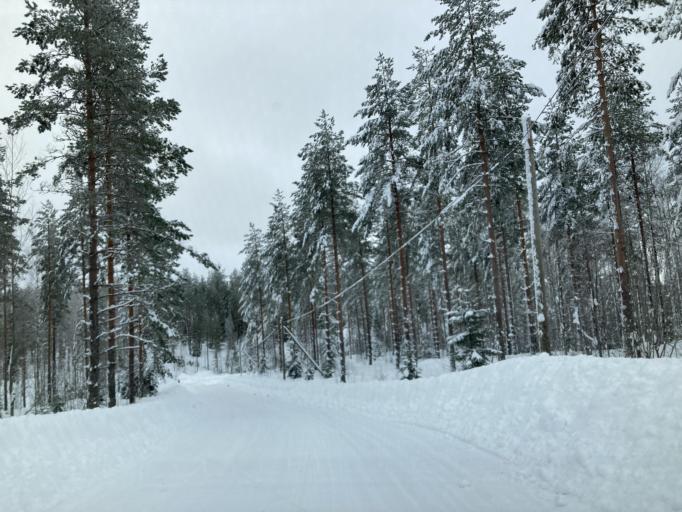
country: FI
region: Central Finland
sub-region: Jaemsae
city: Jaemsae
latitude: 61.8812
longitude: 25.3228
